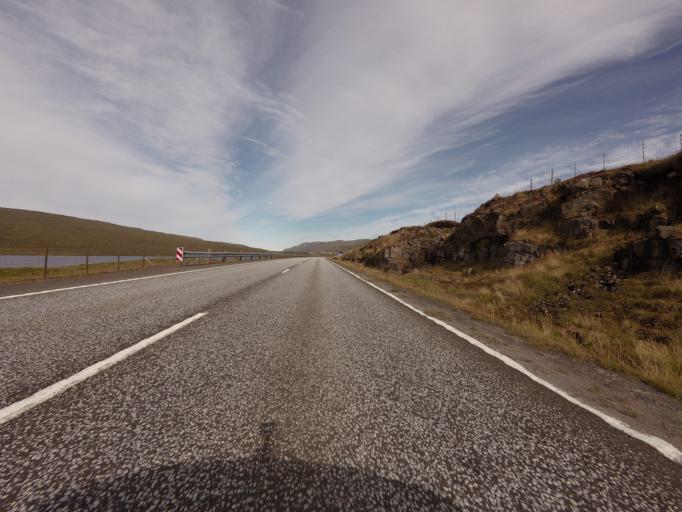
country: FO
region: Vagar
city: Midvagur
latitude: 62.0517
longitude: -7.2295
